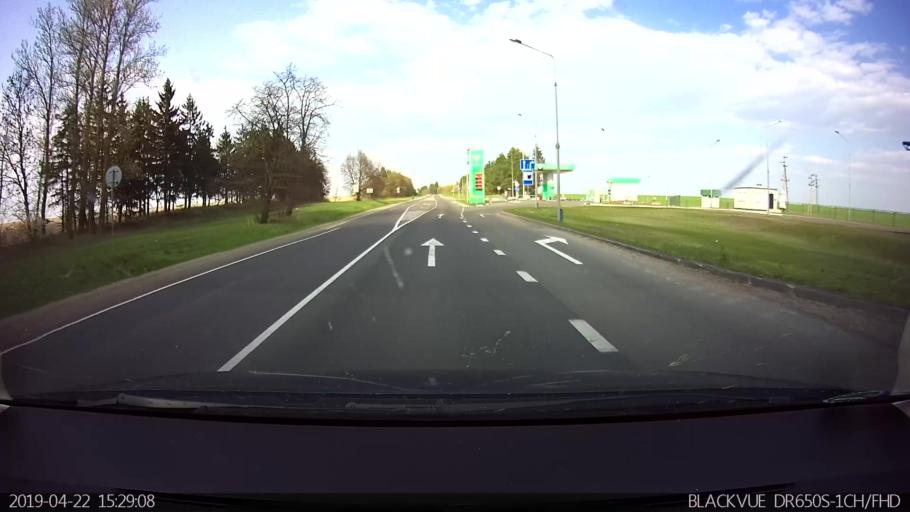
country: BY
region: Brest
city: Vysokaye
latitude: 52.3818
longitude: 23.3712
